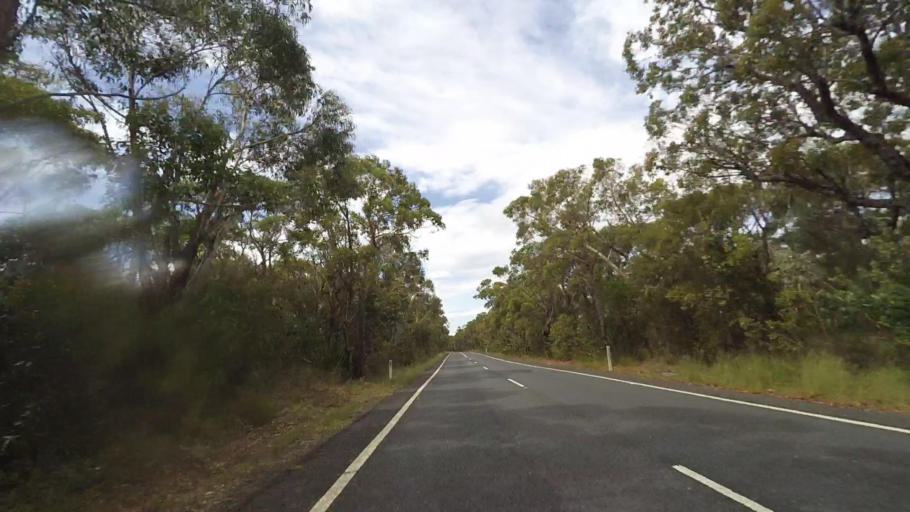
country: AU
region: New South Wales
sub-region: Sutherland Shire
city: Grays Point
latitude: -34.0946
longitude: 151.0618
